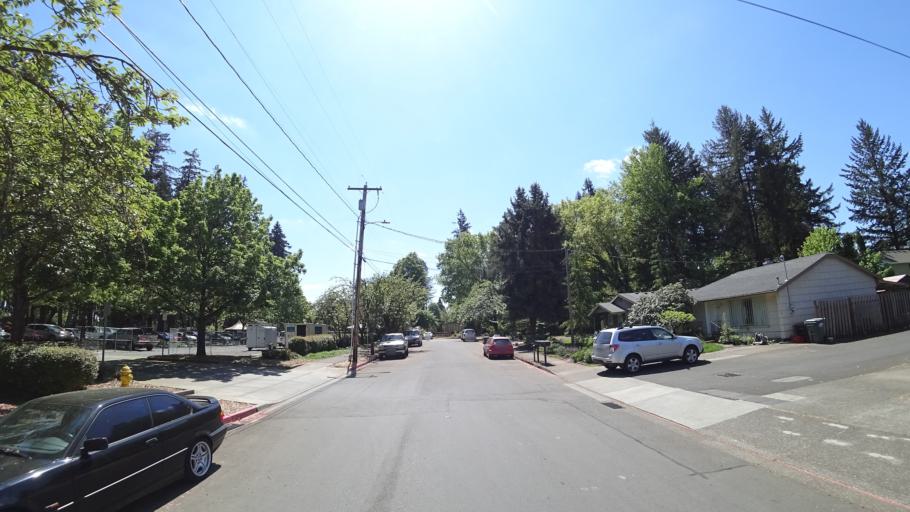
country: US
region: Oregon
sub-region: Washington County
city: Hillsboro
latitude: 45.5143
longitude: -122.9774
